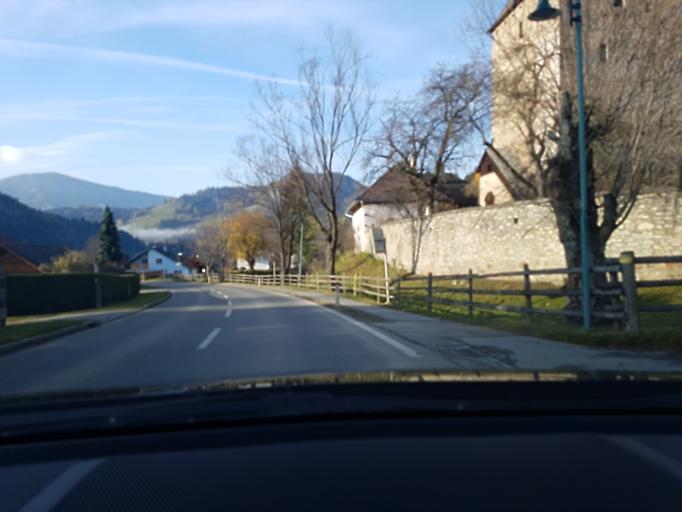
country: AT
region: Styria
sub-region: Politischer Bezirk Murau
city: Schoder
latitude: 47.1899
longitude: 14.1288
